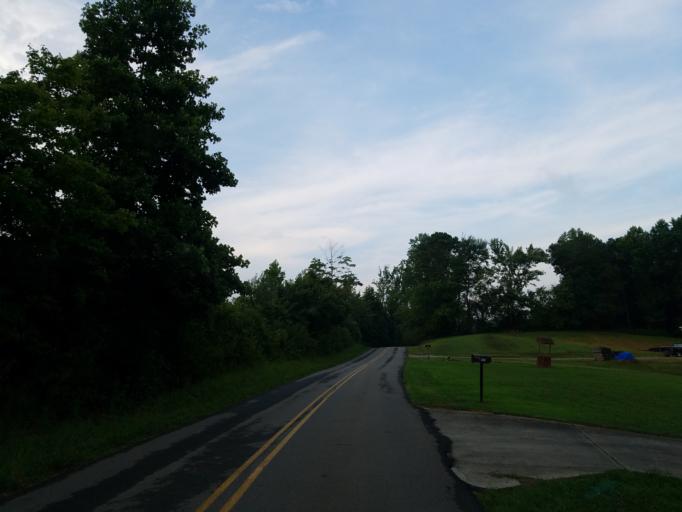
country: US
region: Georgia
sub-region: Pickens County
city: Jasper
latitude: 34.5048
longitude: -84.5279
